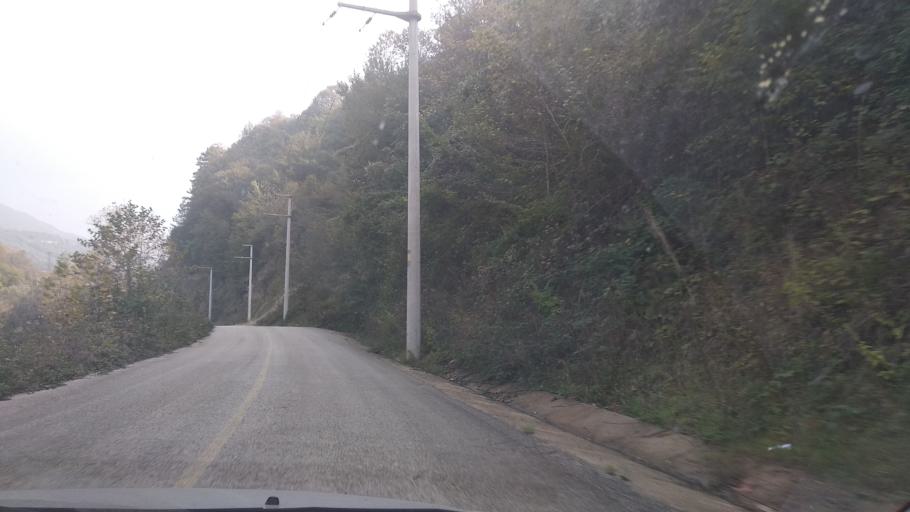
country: TR
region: Duzce
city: Duzce
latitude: 40.7351
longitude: 31.2108
